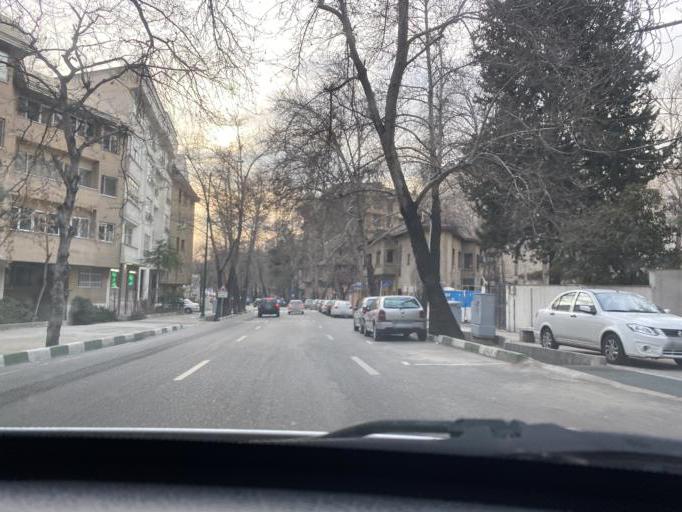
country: IR
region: Tehran
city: Tajrish
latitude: 35.8116
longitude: 51.4477
